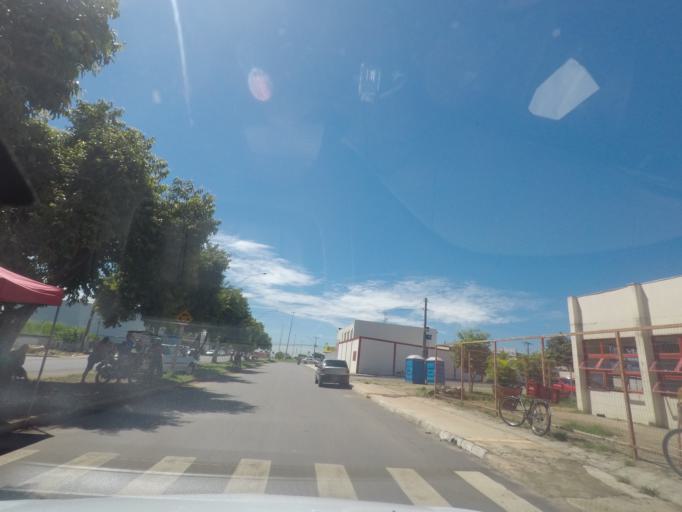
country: BR
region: Goias
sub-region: Aparecida De Goiania
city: Aparecida de Goiania
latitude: -16.7683
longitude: -49.3452
